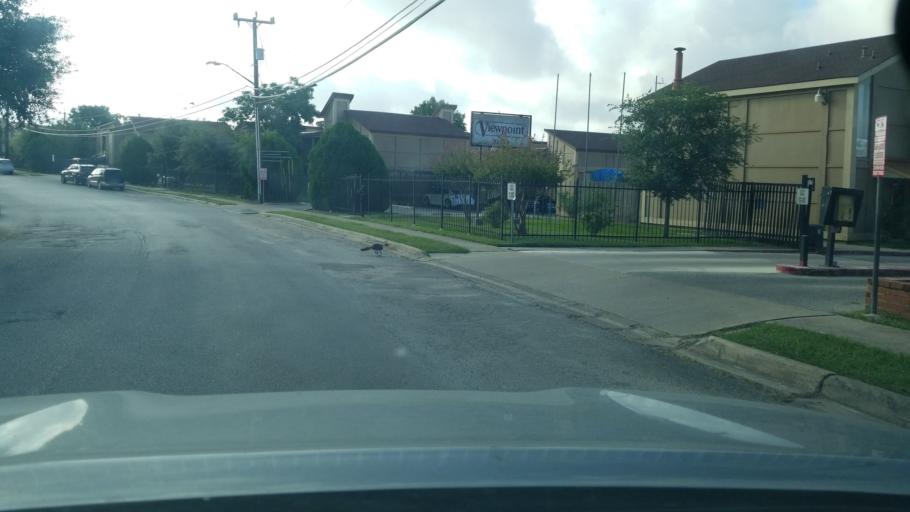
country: US
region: Texas
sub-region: Bexar County
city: Castle Hills
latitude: 29.5333
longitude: -98.4917
